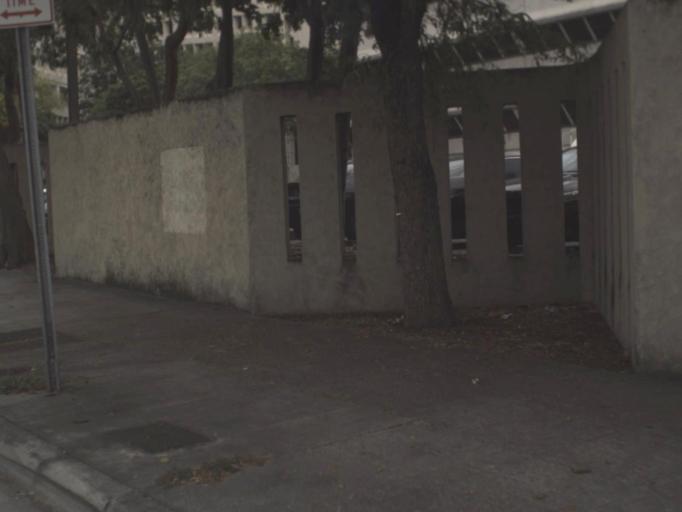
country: US
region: Florida
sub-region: Miami-Dade County
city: Miami
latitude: 25.7788
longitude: -80.1987
